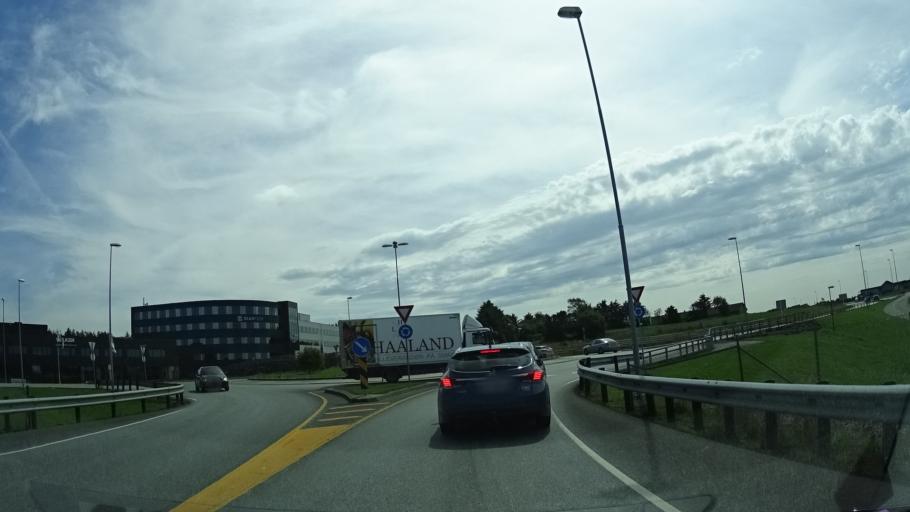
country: NO
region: Rogaland
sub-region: Randaberg
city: Randaberg
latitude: 58.9954
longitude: 5.6505
